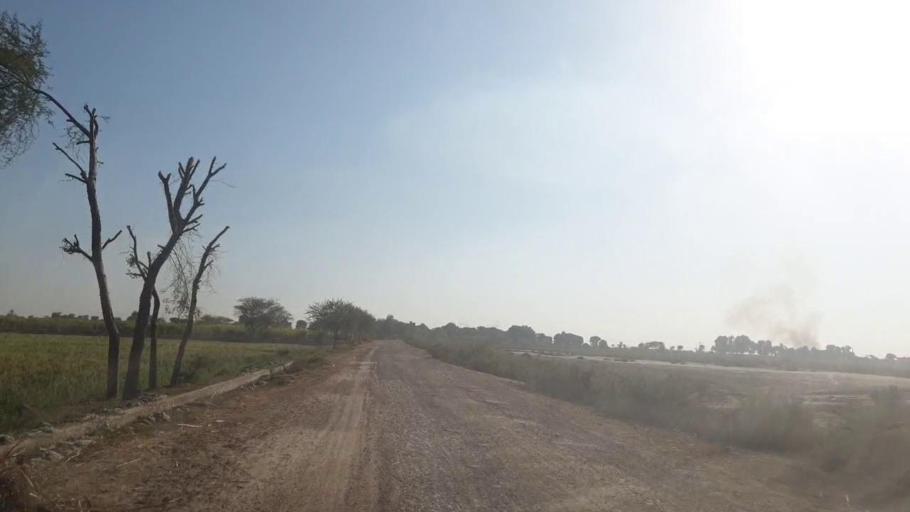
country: PK
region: Sindh
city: Mirwah Gorchani
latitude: 25.4260
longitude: 69.1656
